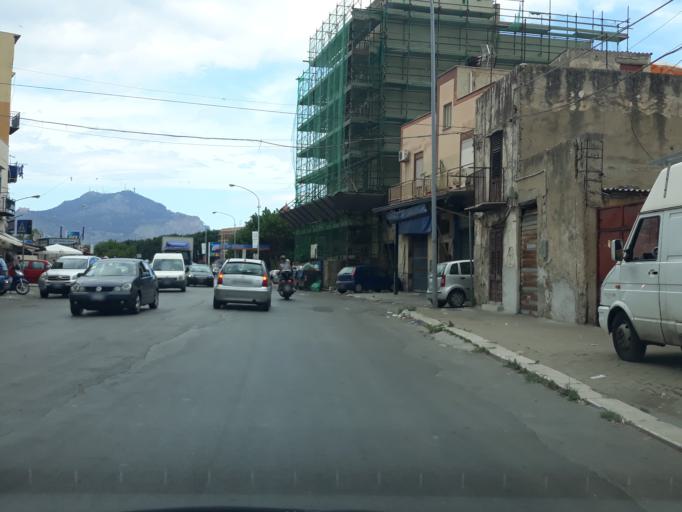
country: IT
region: Sicily
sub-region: Palermo
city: Ciaculli
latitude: 38.1115
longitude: 13.3785
